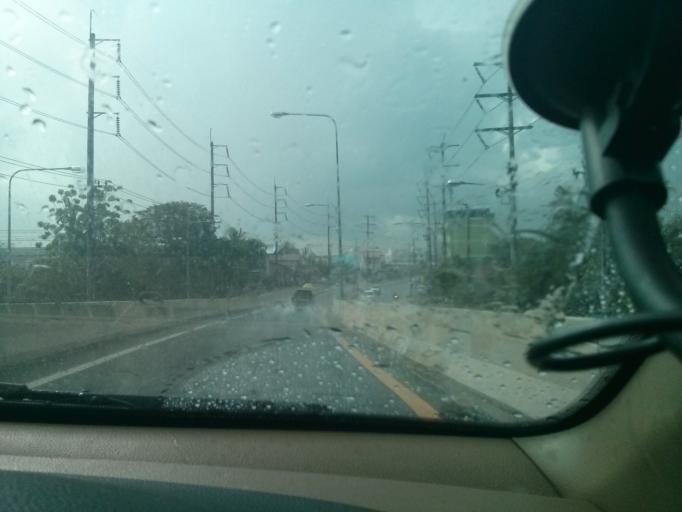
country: TH
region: Nonthaburi
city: Mueang Nonthaburi
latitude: 13.8561
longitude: 100.4944
